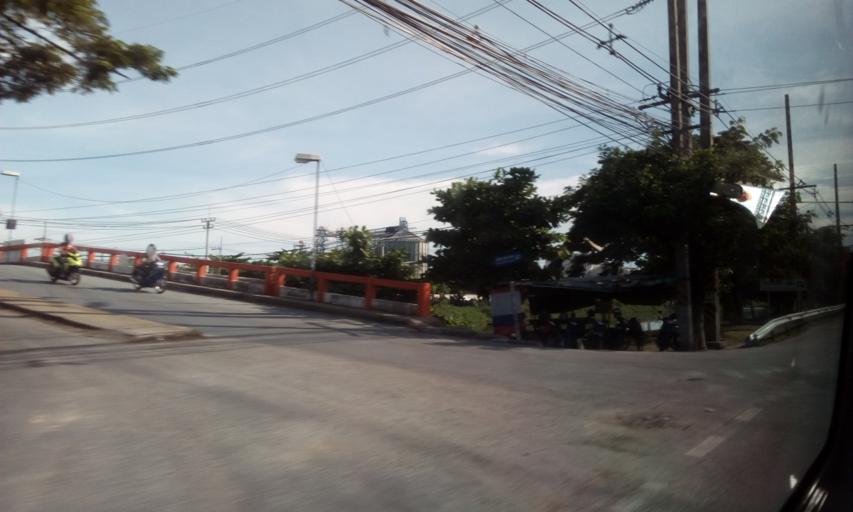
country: TH
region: Bangkok
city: Sai Mai
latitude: 13.9905
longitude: 100.6444
